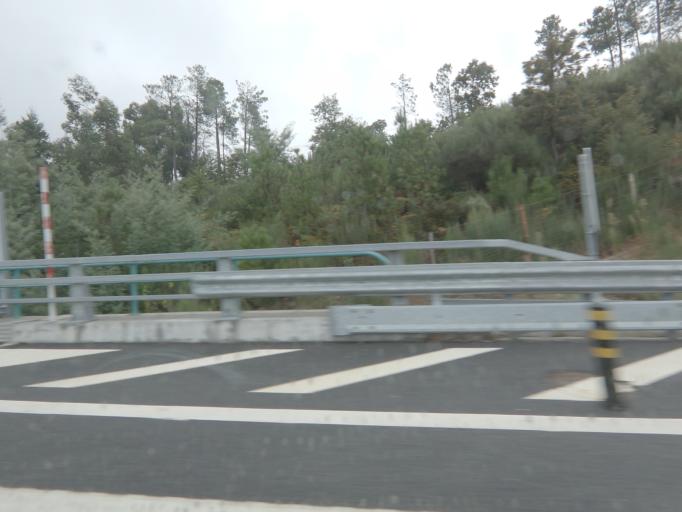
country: PT
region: Vila Real
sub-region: Santa Marta de Penaguiao
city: Santa Marta de Penaguiao
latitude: 41.2793
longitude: -7.8662
